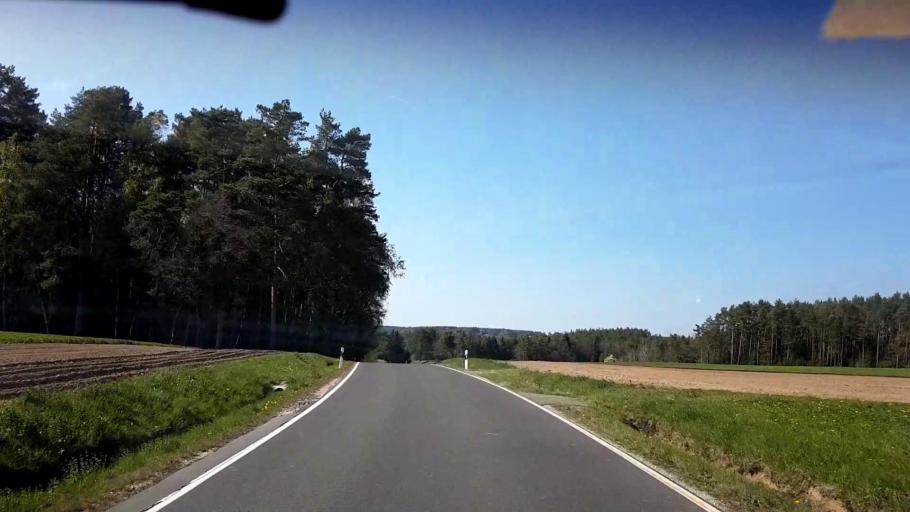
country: DE
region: Bavaria
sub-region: Upper Franconia
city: Pottenstein
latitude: 49.8029
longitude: 11.3733
